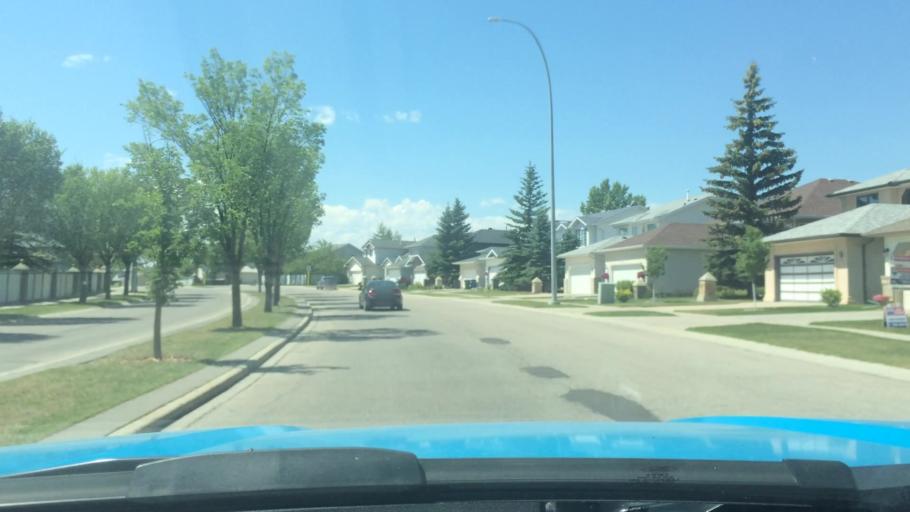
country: CA
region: Alberta
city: Calgary
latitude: 51.1380
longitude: -114.1873
